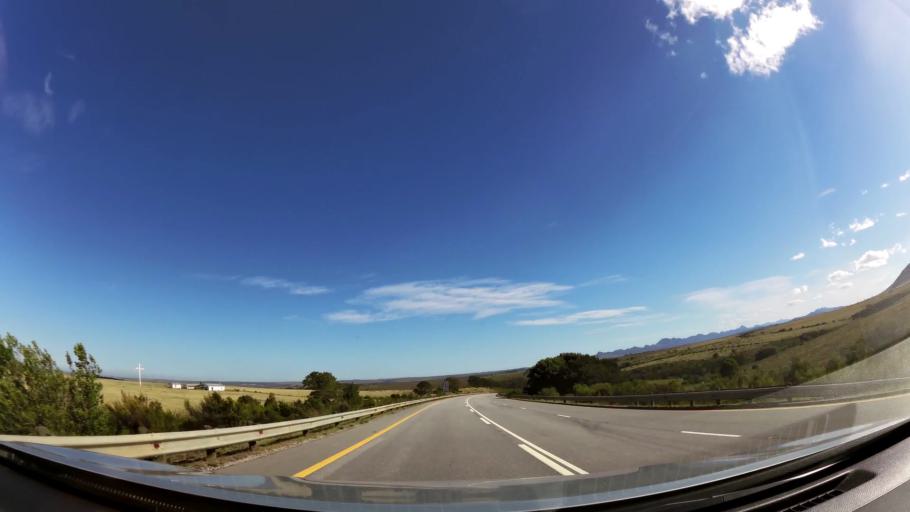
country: ZA
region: Eastern Cape
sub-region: Cacadu District Municipality
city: Kruisfontein
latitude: -34.0044
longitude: 24.6775
